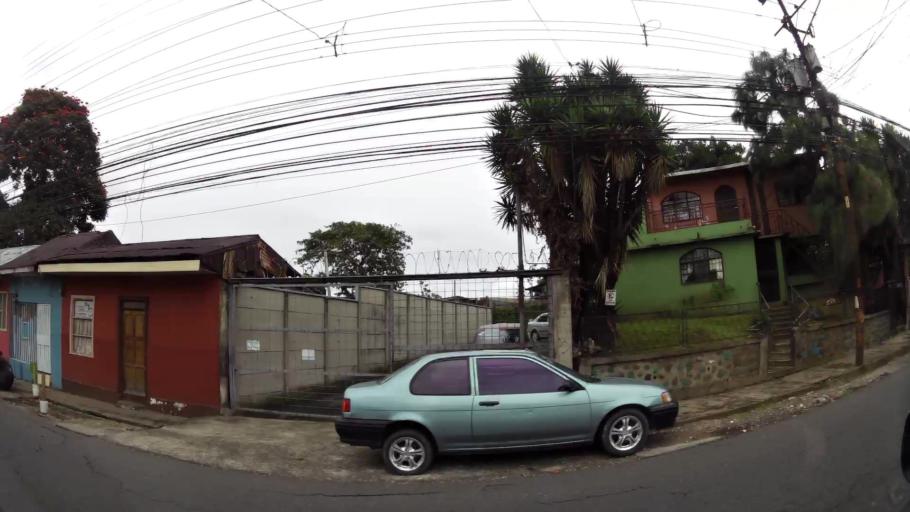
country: CR
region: San Jose
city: Calle Blancos
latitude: 9.9439
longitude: -84.0658
